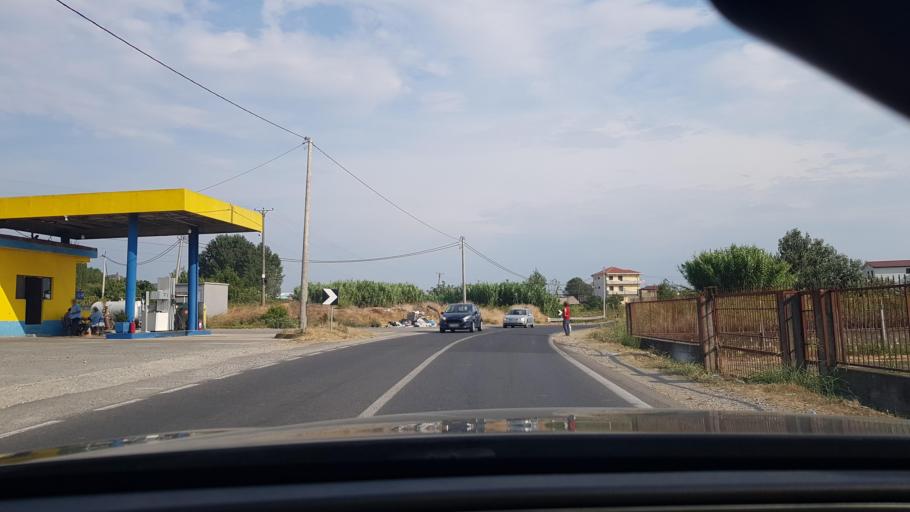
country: AL
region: Durres
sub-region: Rrethi i Durresit
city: Manze
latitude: 41.4483
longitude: 19.5721
